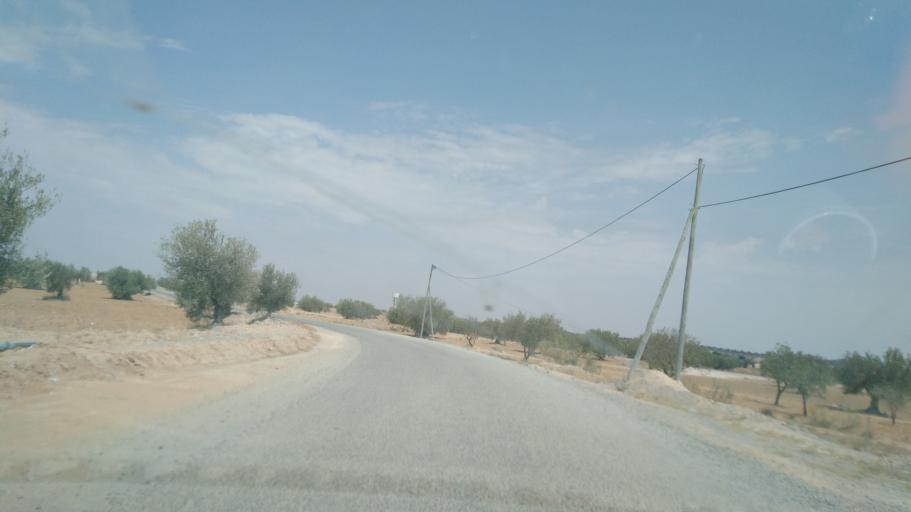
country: TN
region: Safaqis
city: Sfax
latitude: 34.7466
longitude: 10.5611
